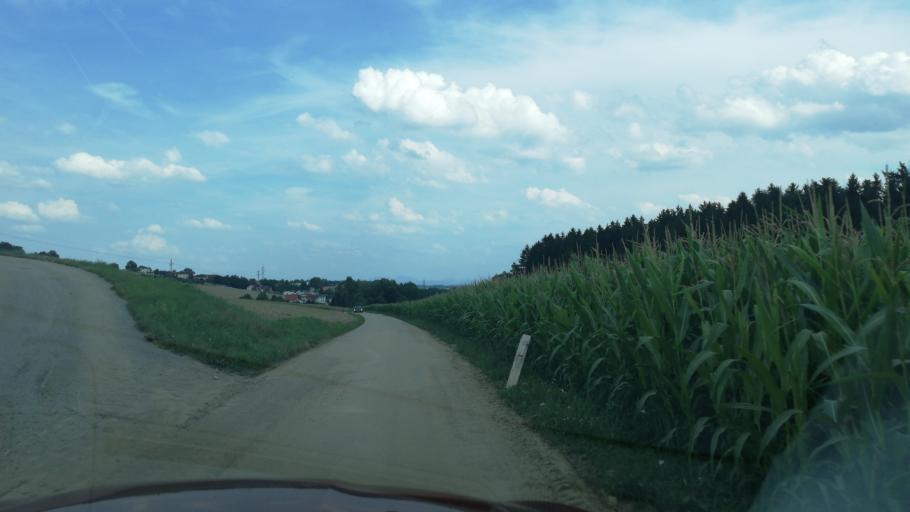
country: AT
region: Upper Austria
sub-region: Wels-Land
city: Pennewang
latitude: 48.1053
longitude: 13.8485
